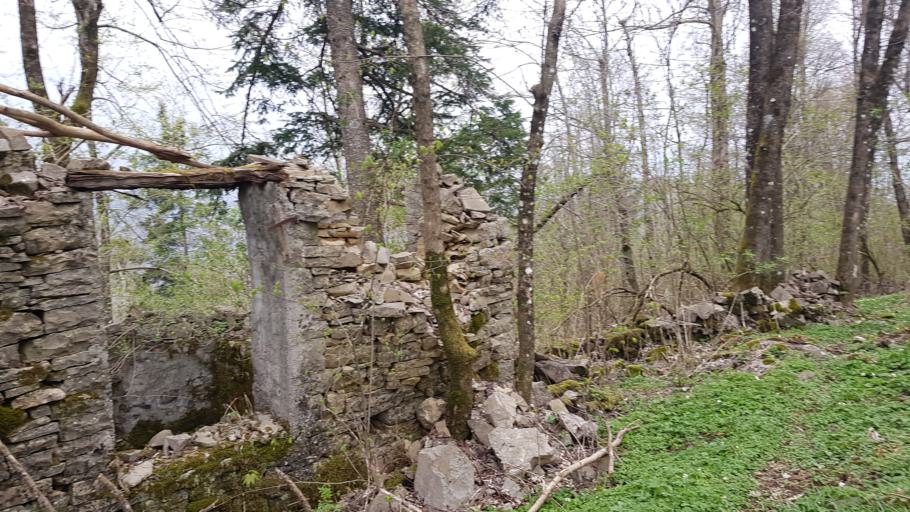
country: IT
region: Friuli Venezia Giulia
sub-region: Provincia di Udine
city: Faedis
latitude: 46.1945
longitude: 13.3869
